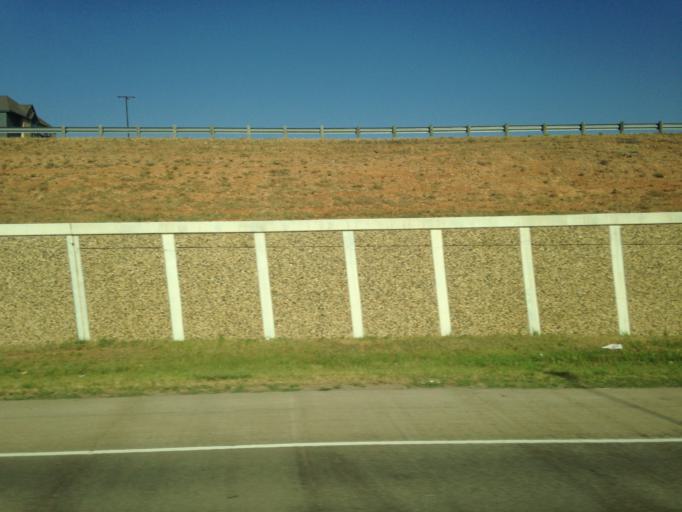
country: US
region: Texas
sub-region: Lubbock County
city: Lubbock
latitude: 33.5518
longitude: -101.8452
